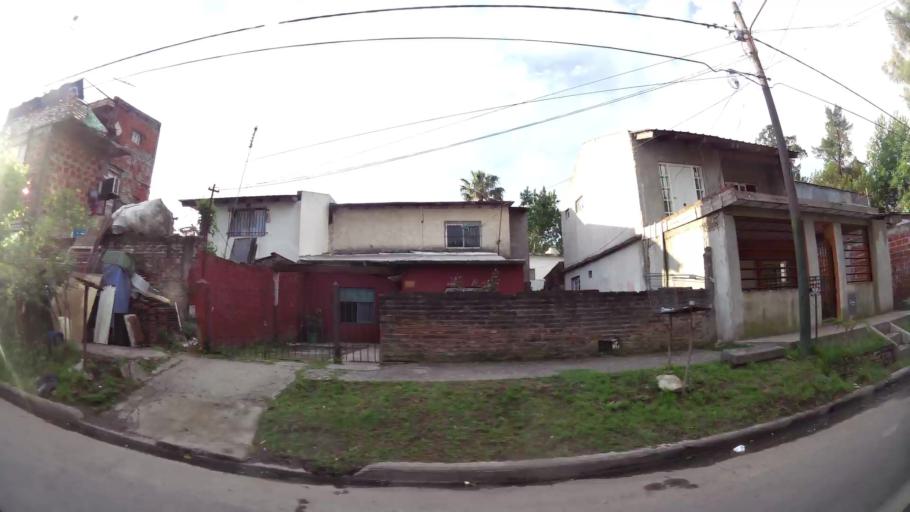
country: AR
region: Buenos Aires
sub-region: Partido de Lomas de Zamora
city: Lomas de Zamora
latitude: -34.7581
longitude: -58.3633
